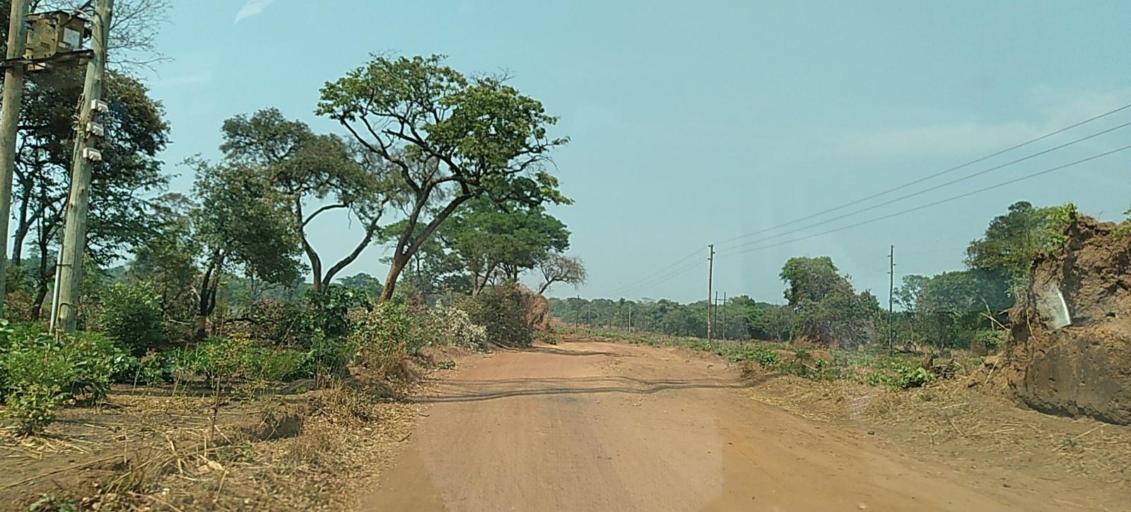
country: ZM
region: Copperbelt
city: Chingola
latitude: -13.0470
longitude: 27.4324
